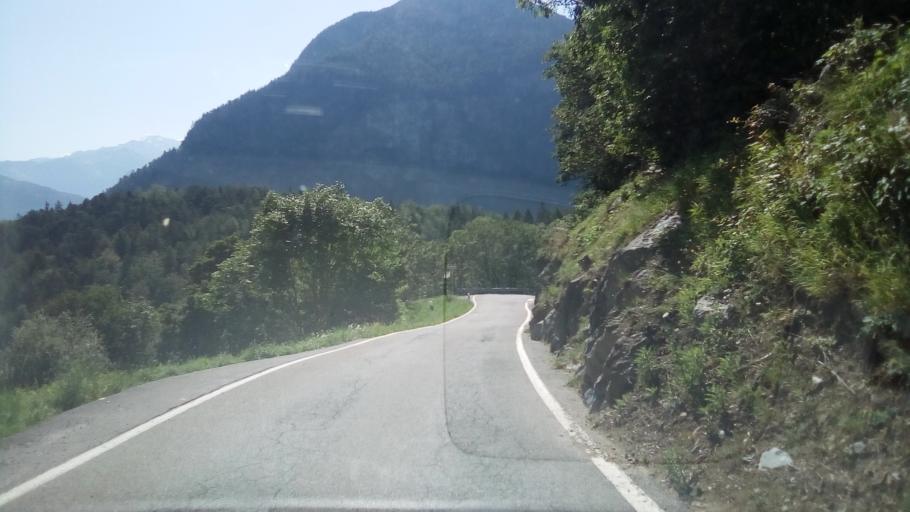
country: CH
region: Valais
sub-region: Saint-Maurice District
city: Salvan
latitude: 46.1261
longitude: 7.0237
